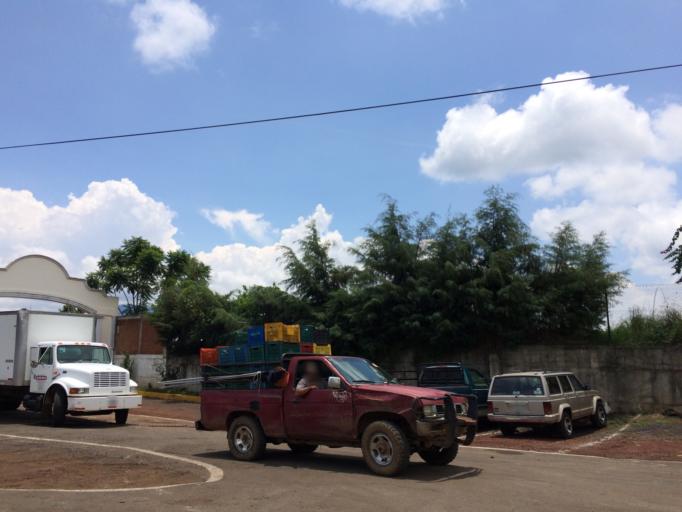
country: MX
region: Michoacan
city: Periban de Ramos
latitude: 19.5352
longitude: -102.4118
